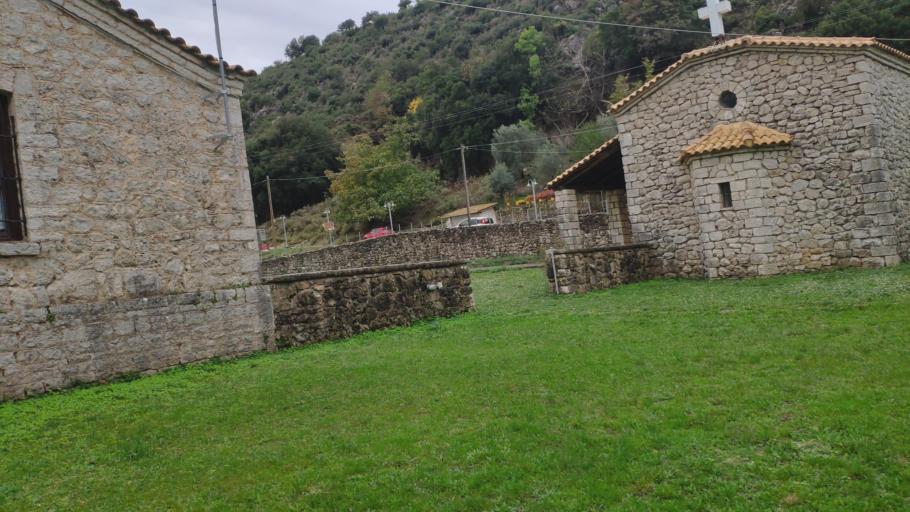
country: GR
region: Epirus
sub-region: Nomos Prevezis
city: Kanalaki
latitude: 39.3598
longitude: 20.6414
